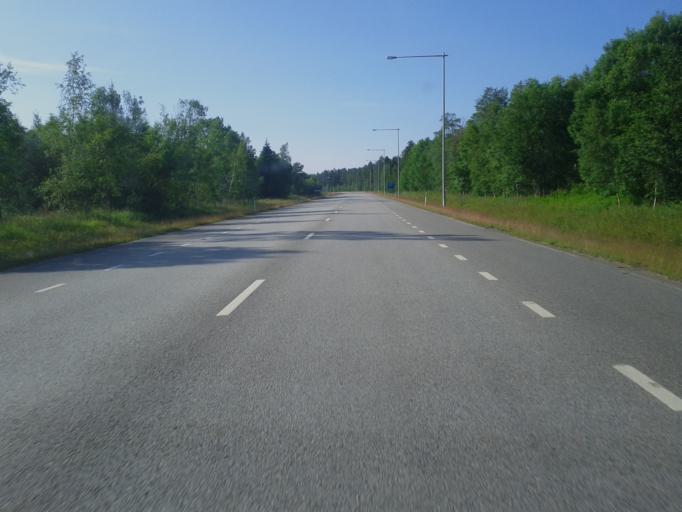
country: SE
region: Vaesterbotten
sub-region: Umea Kommun
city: Umea
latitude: 63.7887
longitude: 20.3006
